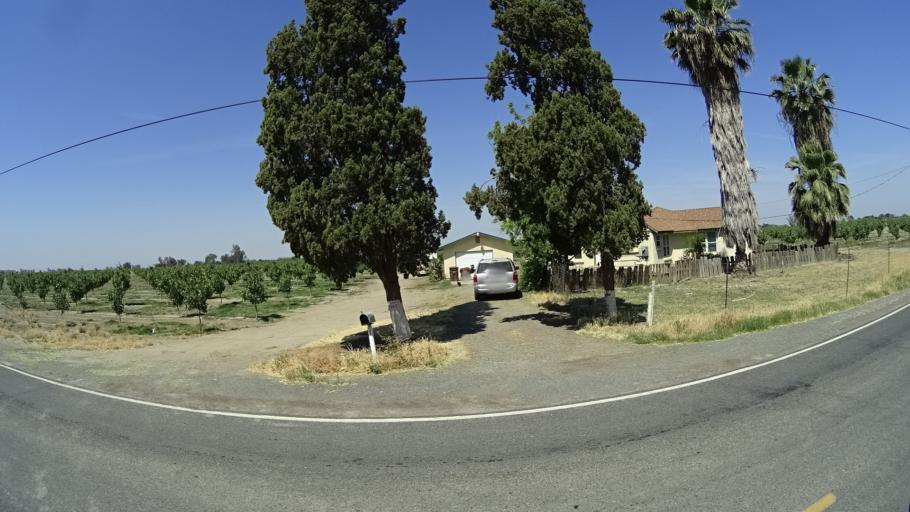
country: US
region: California
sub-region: Fresno County
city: Riverdale
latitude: 36.3731
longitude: -119.8514
